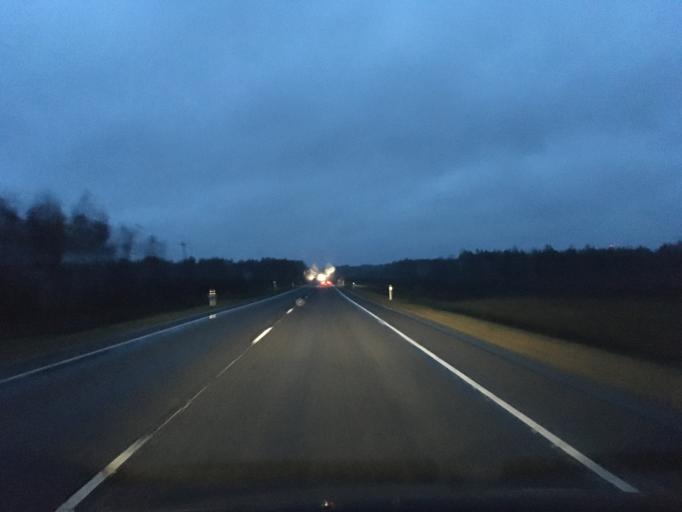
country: EE
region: Harju
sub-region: Nissi vald
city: Turba
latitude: 58.9838
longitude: 24.0577
